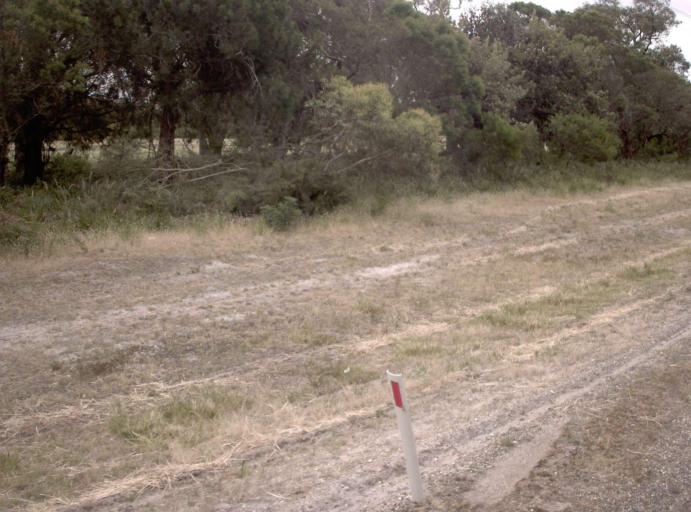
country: AU
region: Victoria
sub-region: East Gippsland
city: Bairnsdale
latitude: -38.0609
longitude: 147.5635
